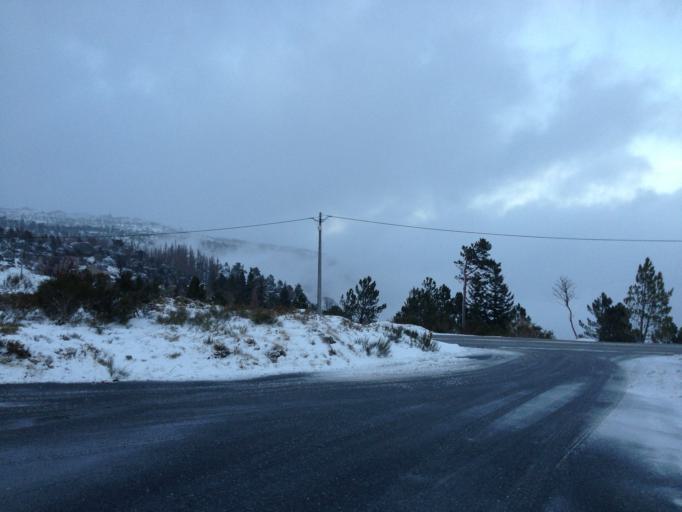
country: PT
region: Castelo Branco
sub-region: Covilha
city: Covilha
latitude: 40.2930
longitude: -7.5368
